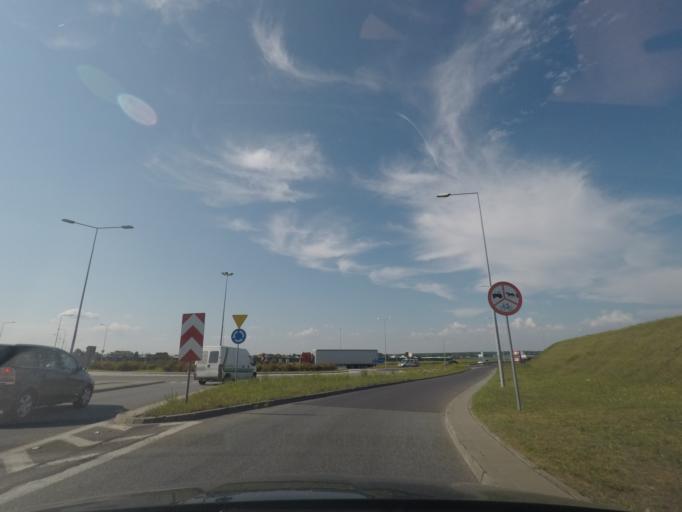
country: PL
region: Silesian Voivodeship
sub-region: Zory
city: Zory
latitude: 50.0639
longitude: 18.6609
